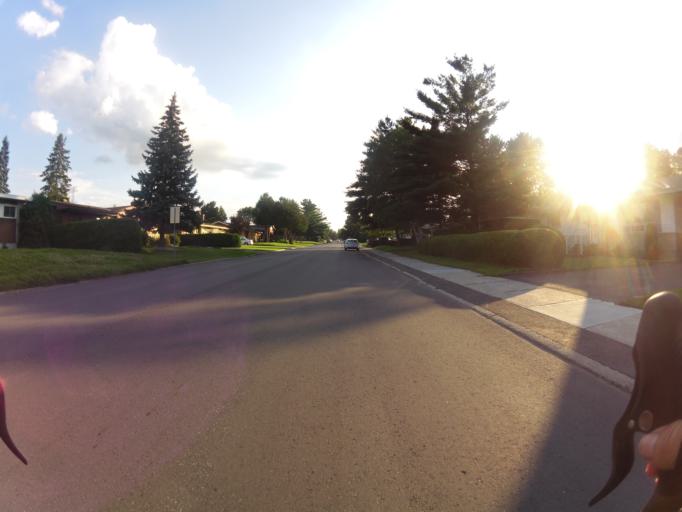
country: CA
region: Ontario
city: Bells Corners
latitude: 45.3305
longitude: -75.7546
